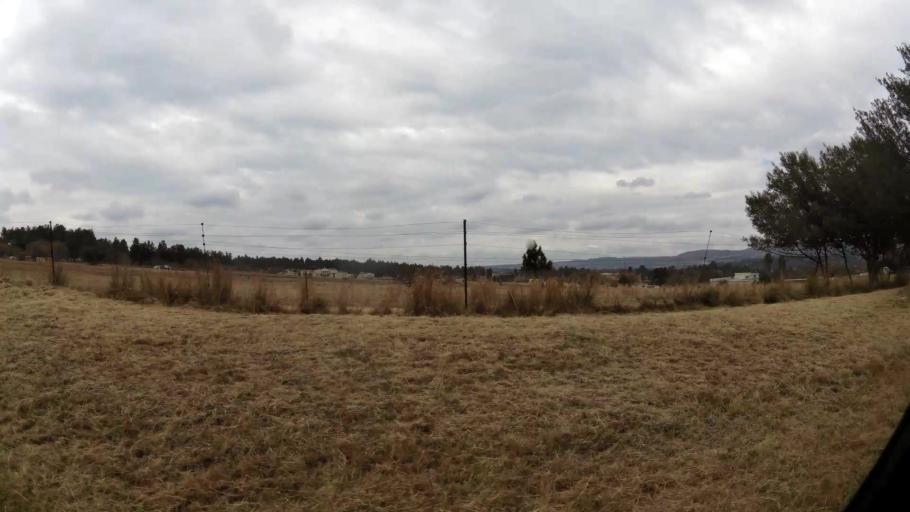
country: ZA
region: Gauteng
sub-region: West Rand District Municipality
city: Muldersdriseloop
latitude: -26.0555
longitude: 27.8860
